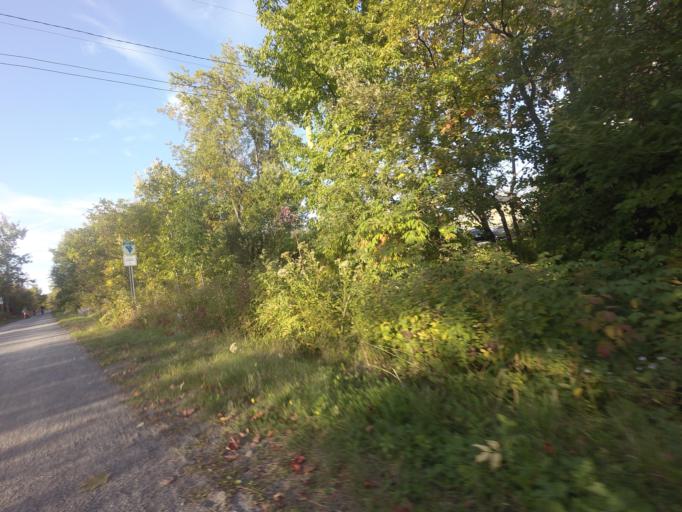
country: CA
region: Quebec
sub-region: Laurentides
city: Prevost
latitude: 45.8412
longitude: -74.0596
